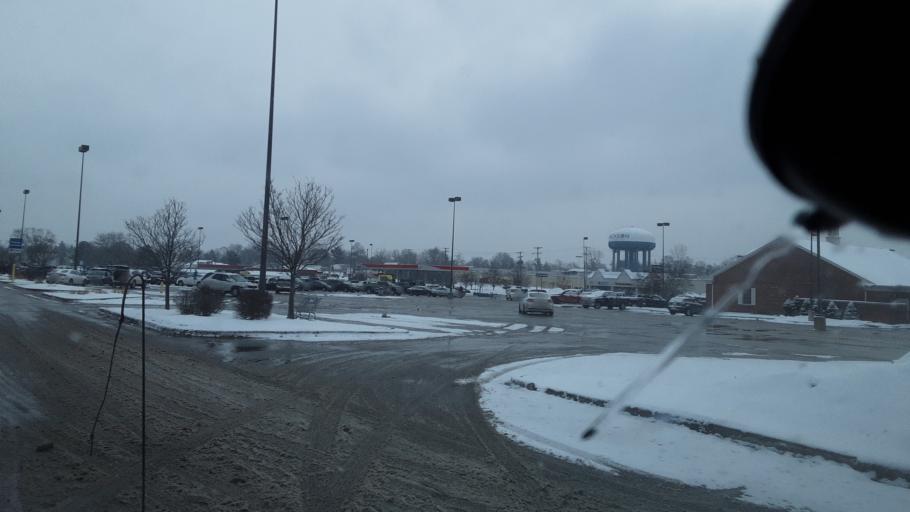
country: US
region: Michigan
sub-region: Jackson County
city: Jackson
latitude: 42.2633
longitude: -84.4281
